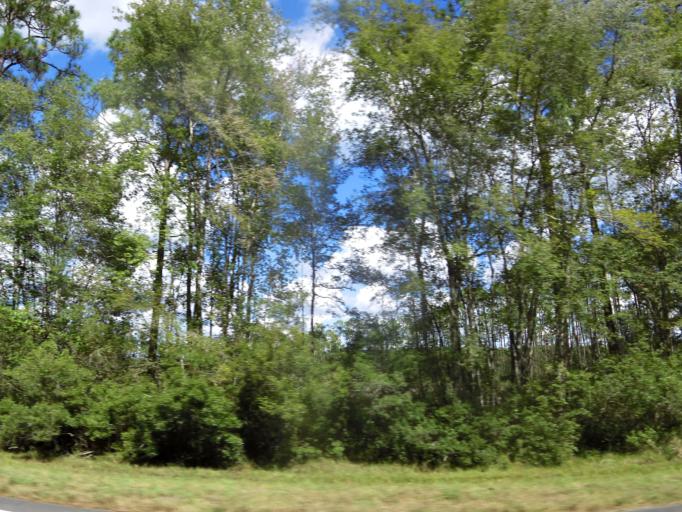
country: US
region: Georgia
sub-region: Clinch County
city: Homerville
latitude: 30.7324
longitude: -82.5883
